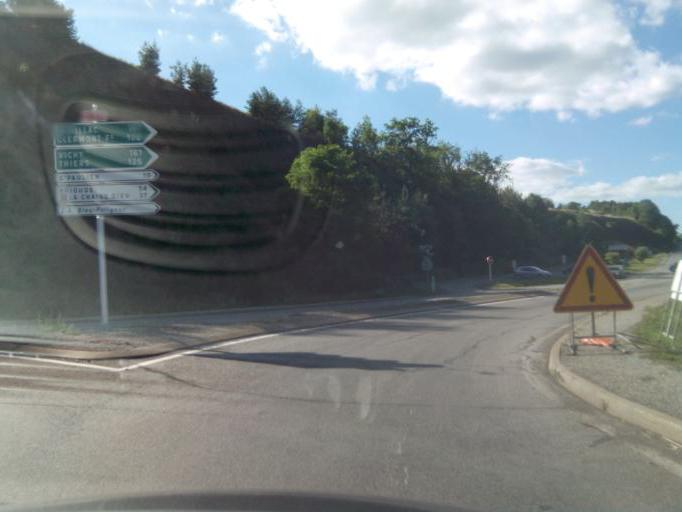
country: FR
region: Auvergne
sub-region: Departement de la Haute-Loire
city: Polignac
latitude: 45.0664
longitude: 3.8507
